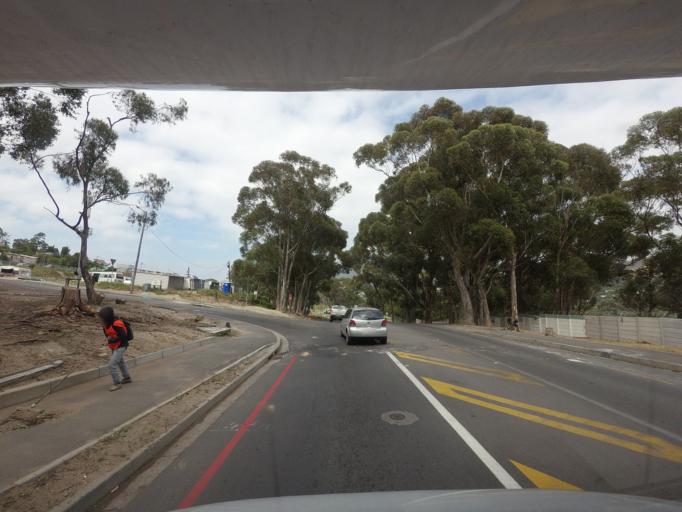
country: ZA
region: Western Cape
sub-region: City of Cape Town
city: Constantia
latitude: -34.0241
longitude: 18.3622
